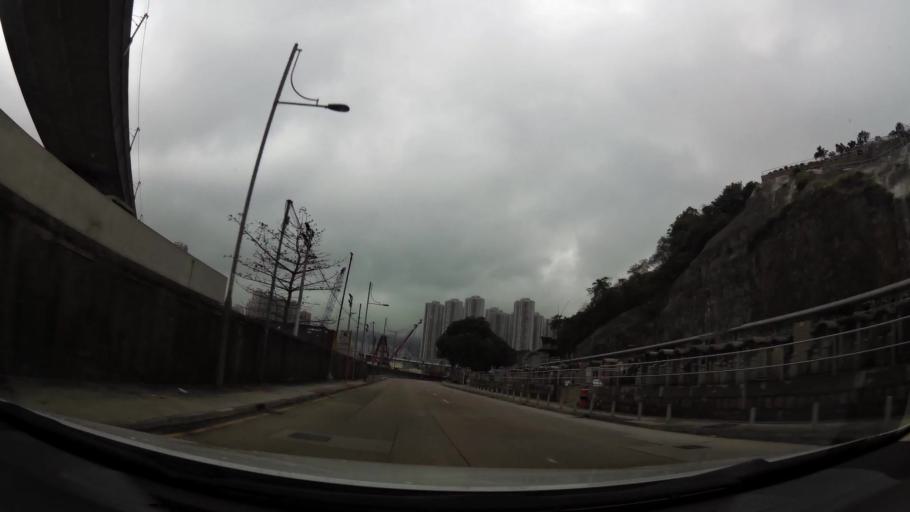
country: HK
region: Tsuen Wan
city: Tsuen Wan
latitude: 22.3560
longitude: 114.1157
